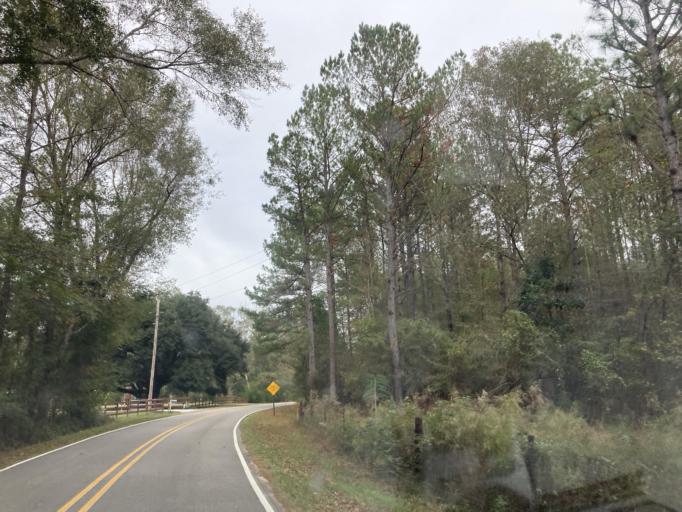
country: US
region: Mississippi
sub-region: Lamar County
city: Purvis
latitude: 31.0930
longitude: -89.3782
